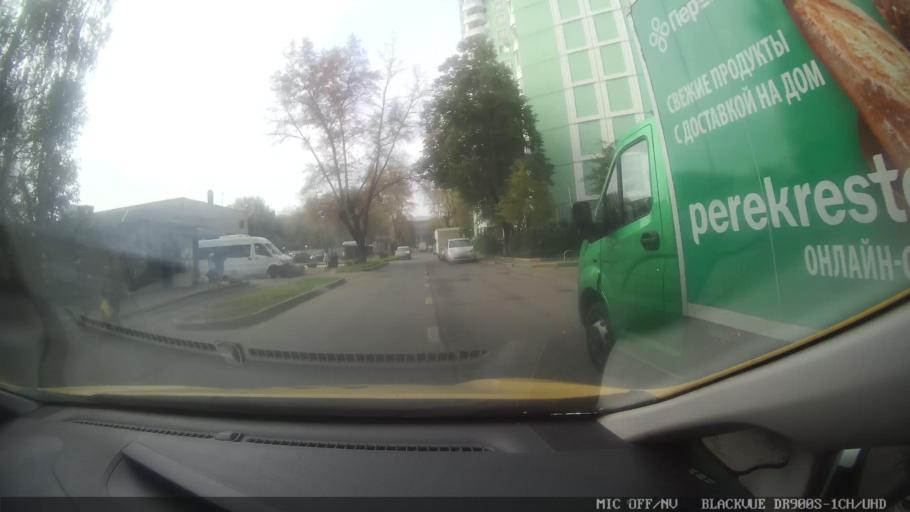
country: RU
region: Moskovskaya
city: Lyubertsy
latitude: 55.6878
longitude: 37.8790
